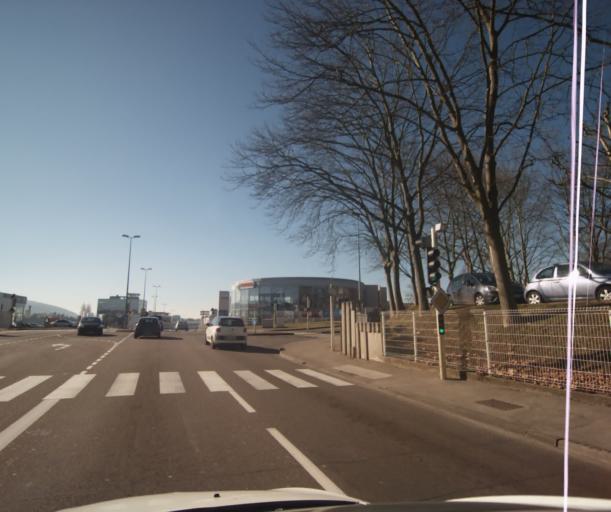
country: FR
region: Franche-Comte
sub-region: Departement du Doubs
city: Besancon
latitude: 47.2434
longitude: 5.9951
